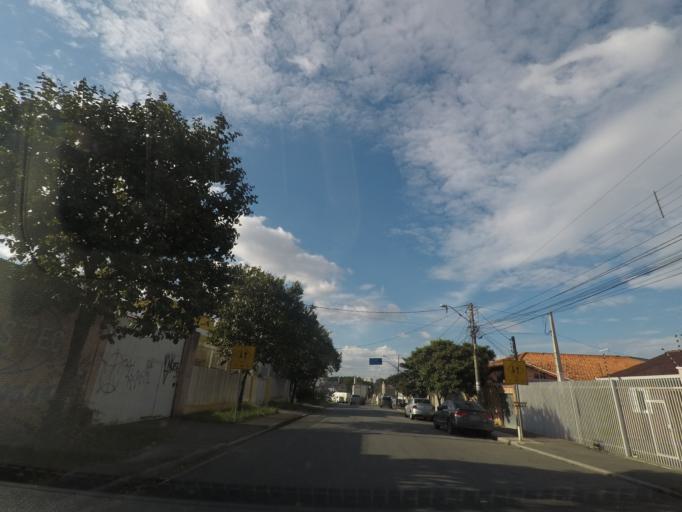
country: BR
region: Parana
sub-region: Sao Jose Dos Pinhais
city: Sao Jose dos Pinhais
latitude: -25.5019
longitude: -49.2760
